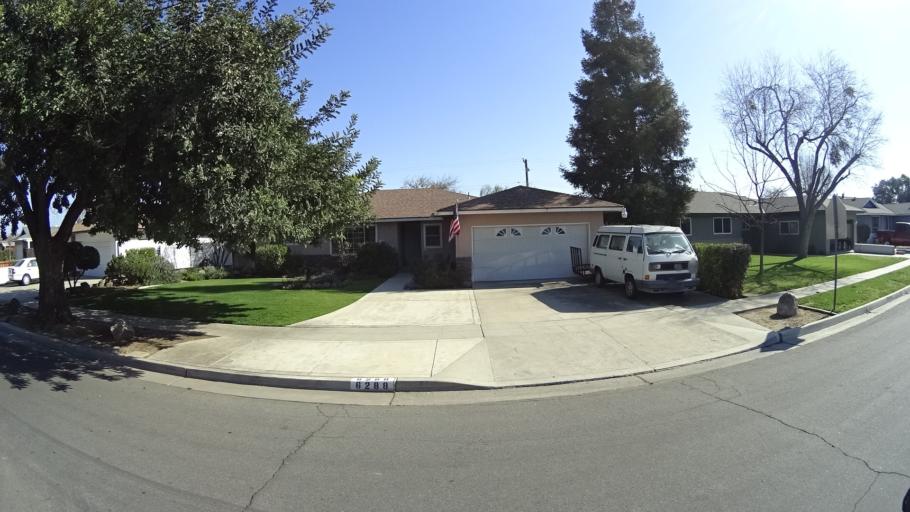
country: US
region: California
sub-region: Fresno County
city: Clovis
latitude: 36.8282
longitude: -119.7767
